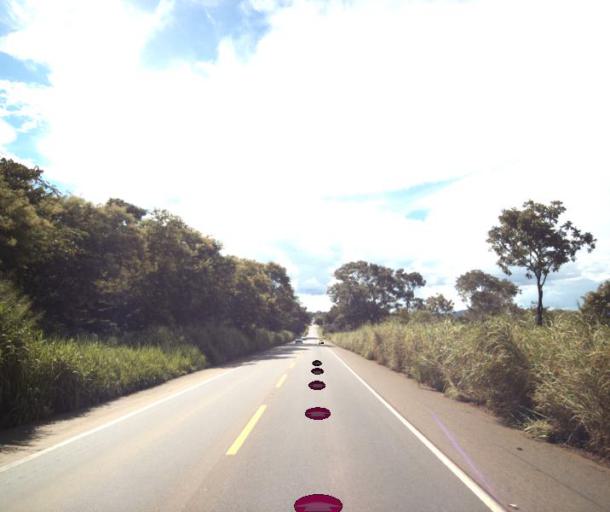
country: BR
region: Goias
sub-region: Jaragua
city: Jaragua
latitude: -15.7916
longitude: -49.3020
